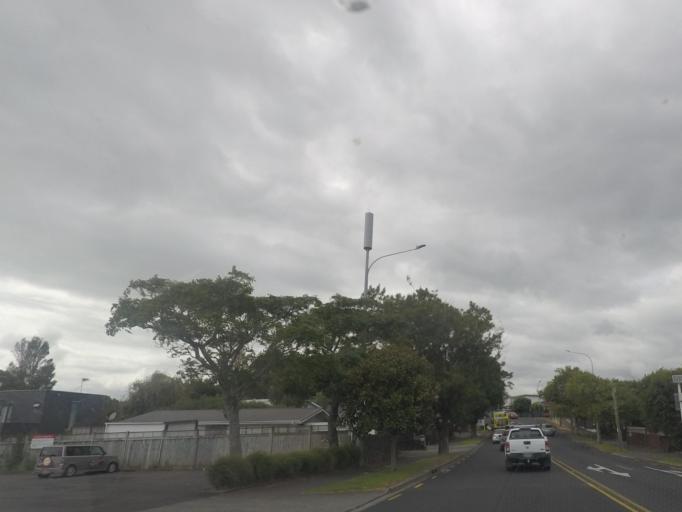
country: NZ
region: Auckland
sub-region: Auckland
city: Tamaki
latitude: -36.8635
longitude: 174.8410
